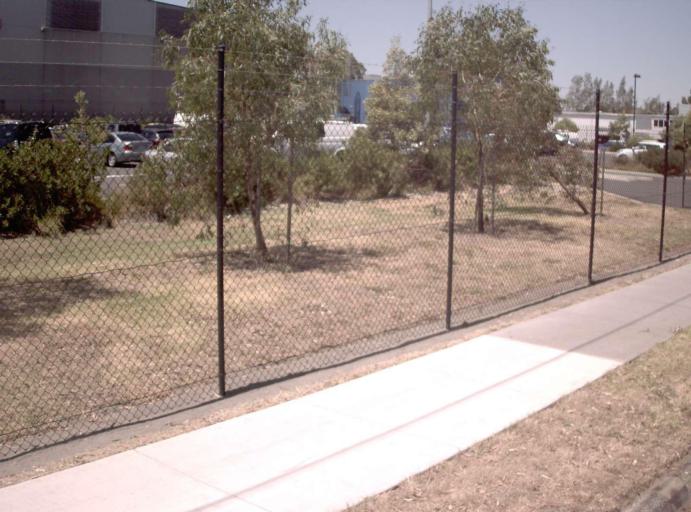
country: AU
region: Victoria
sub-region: Monash
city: Notting Hill
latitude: -37.8864
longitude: 145.1647
